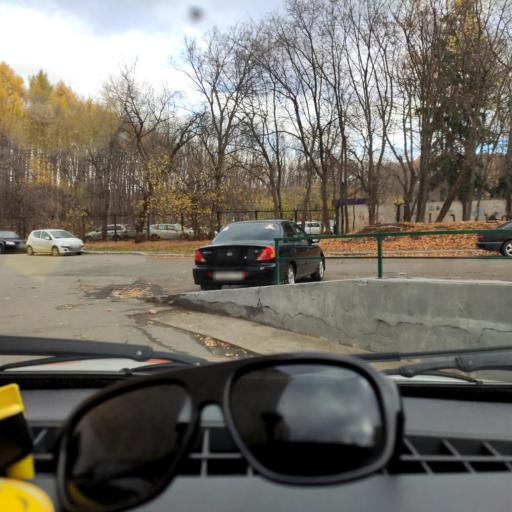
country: RU
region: Bashkortostan
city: Ufa
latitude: 54.7181
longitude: 56.0145
